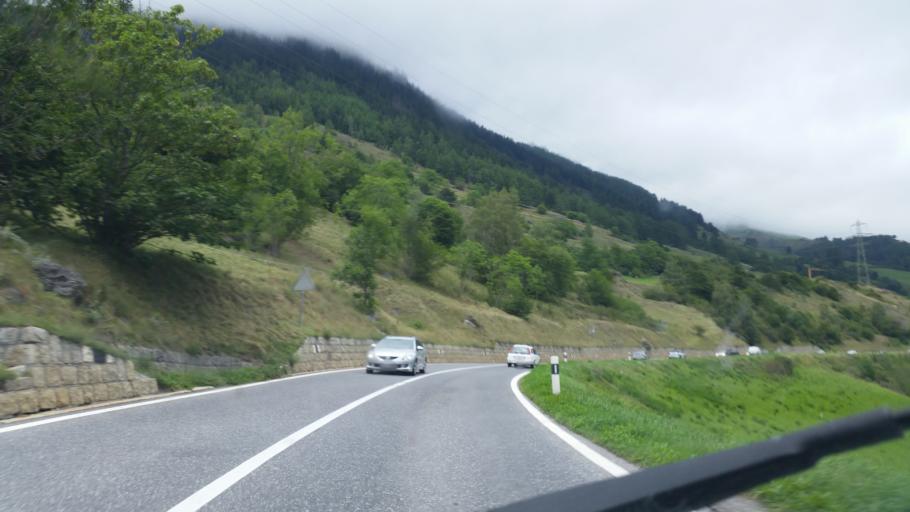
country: CH
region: Valais
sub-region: Entremont District
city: Orsieres
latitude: 46.0161
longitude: 7.1620
